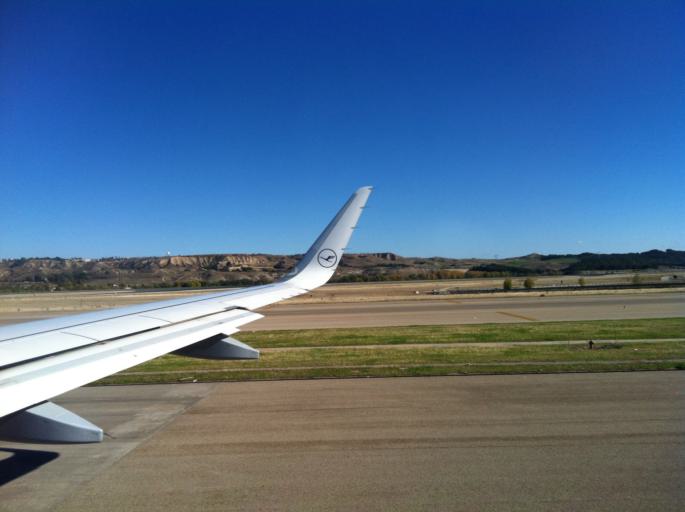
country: ES
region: Madrid
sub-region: Provincia de Madrid
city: Barajas de Madrid
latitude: 40.4909
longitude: -3.5625
